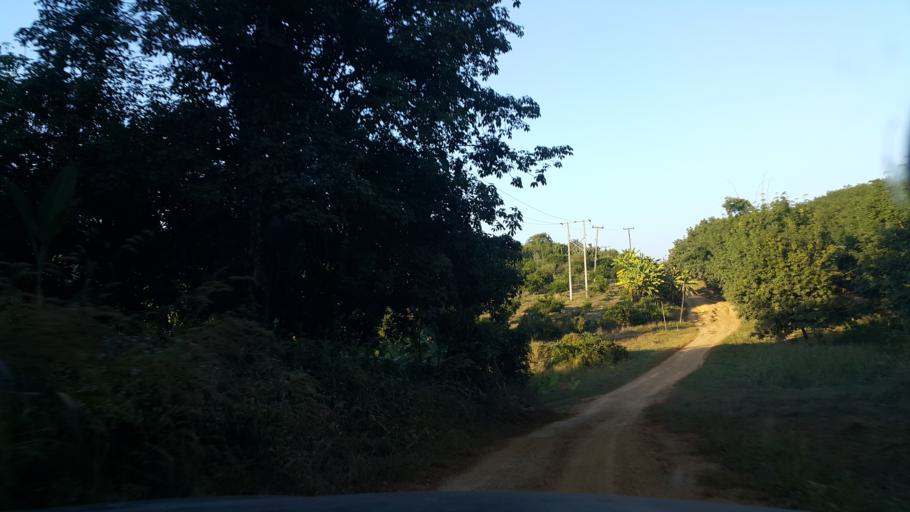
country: TH
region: Sukhothai
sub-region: Amphoe Si Satchanalai
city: Si Satchanalai
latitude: 17.6019
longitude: 99.6136
